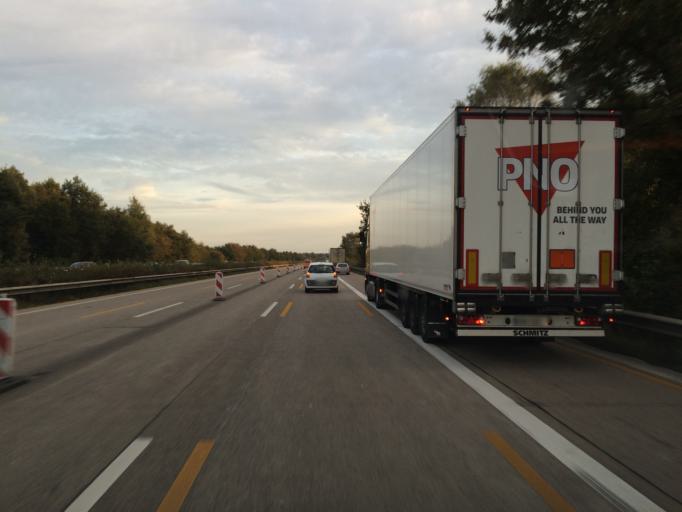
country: DE
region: Lower Saxony
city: Hademstorf
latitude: 52.7263
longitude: 9.6782
